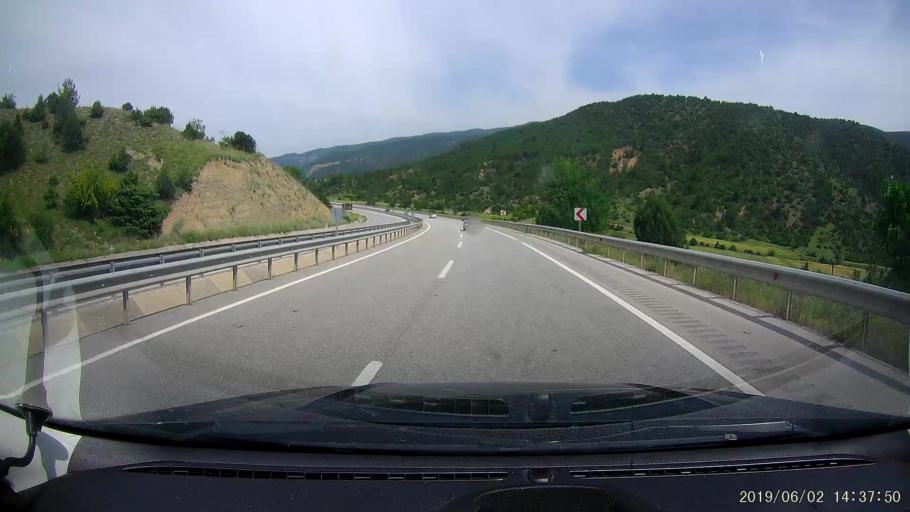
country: TR
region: Corum
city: Hacihamza
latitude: 41.0505
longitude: 34.2661
